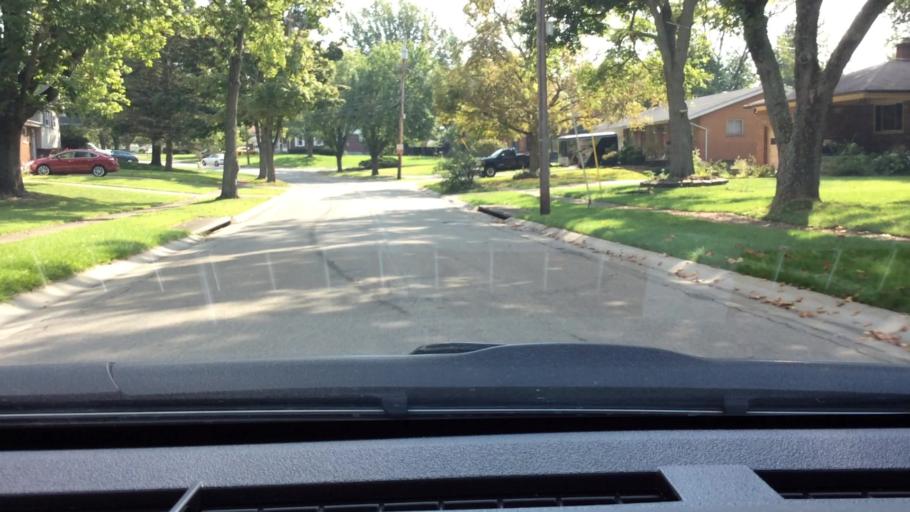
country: US
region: Ohio
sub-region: Hamilton County
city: Greenhills
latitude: 39.2692
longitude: -84.5020
